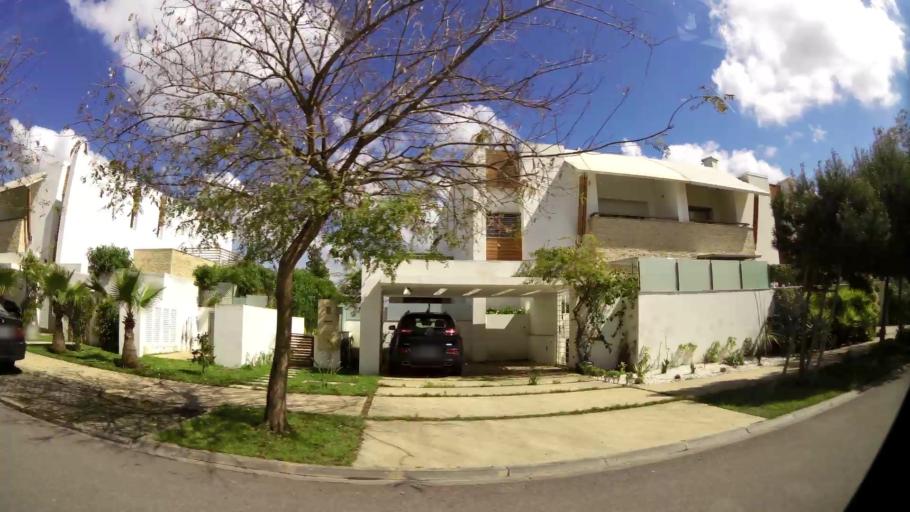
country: MA
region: Grand Casablanca
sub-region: Nouaceur
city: Bouskoura
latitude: 33.4943
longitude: -7.6004
